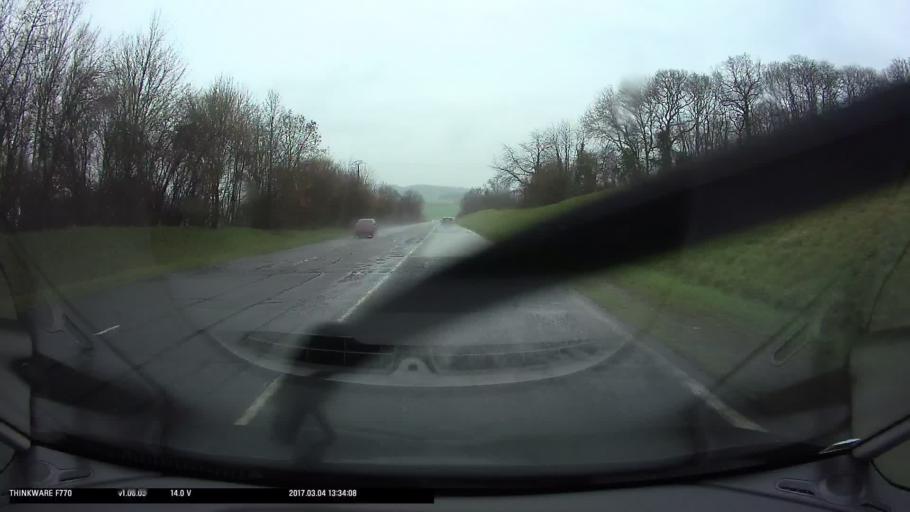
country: FR
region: Ile-de-France
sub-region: Departement du Val-d'Oise
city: Marines
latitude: 49.1230
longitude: 2.0076
